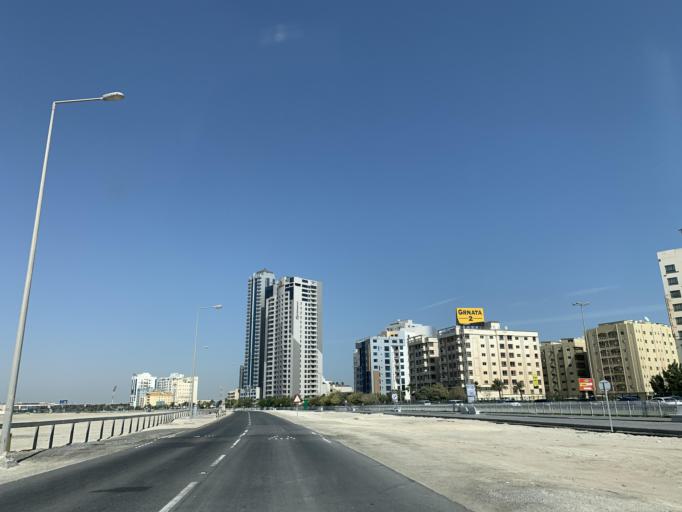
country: BH
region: Manama
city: Manama
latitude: 26.2017
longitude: 50.5832
